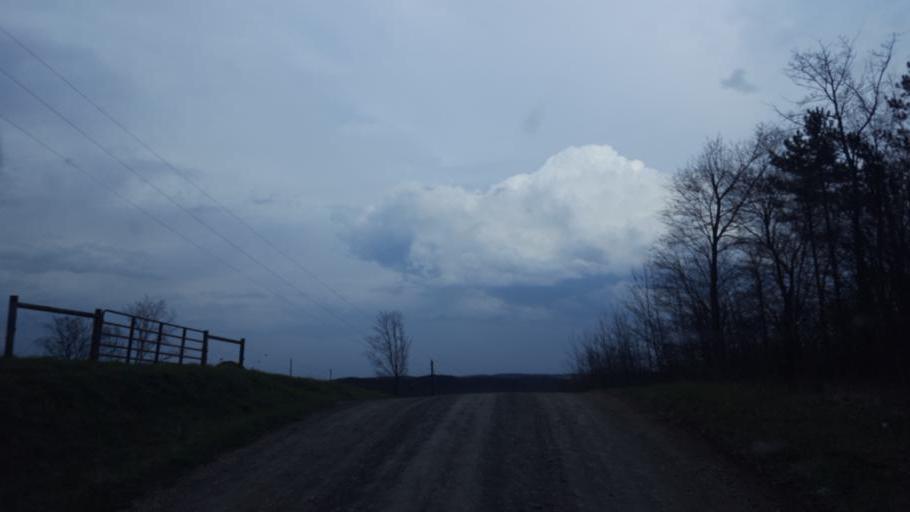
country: US
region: Ohio
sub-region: Guernsey County
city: Mantua
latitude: 40.1252
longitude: -81.7892
